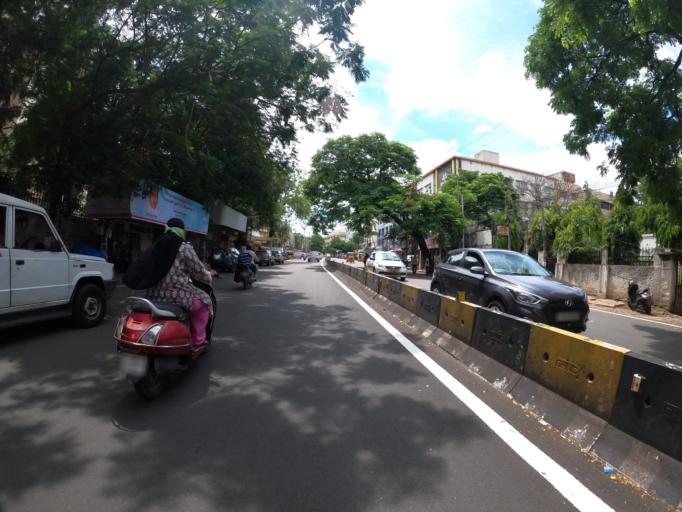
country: IN
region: Telangana
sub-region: Hyderabad
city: Hyderabad
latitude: 17.3979
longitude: 78.4827
